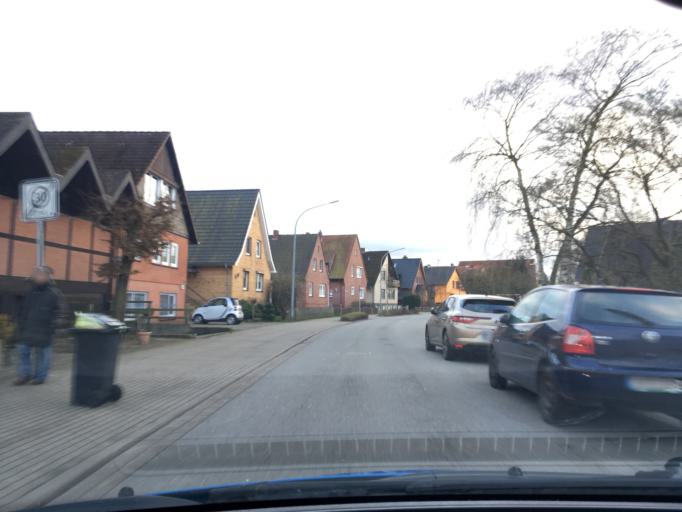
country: DE
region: Lower Saxony
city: Winsen
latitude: 53.3624
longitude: 10.2152
